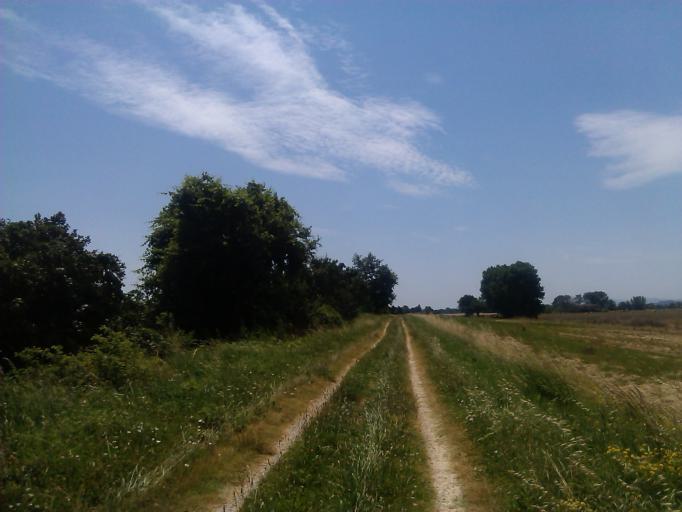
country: IT
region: Tuscany
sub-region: Province of Arezzo
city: Cesa
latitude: 43.3309
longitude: 11.8311
